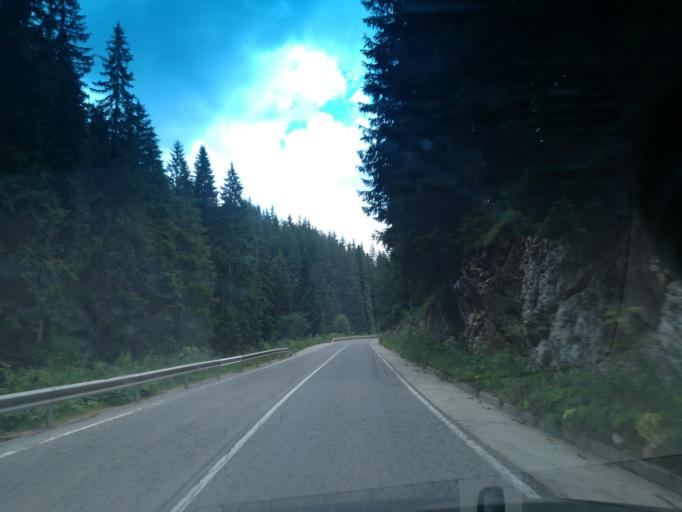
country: BG
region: Smolyan
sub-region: Obshtina Chepelare
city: Chepelare
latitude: 41.6649
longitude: 24.7145
